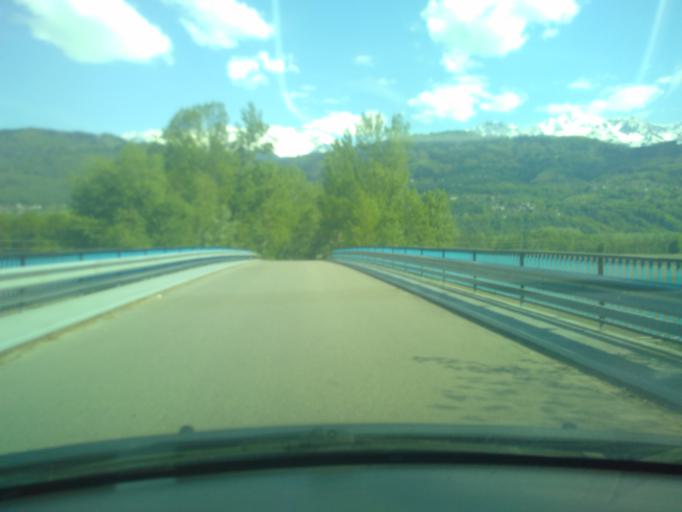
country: FR
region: Rhone-Alpes
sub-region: Departement de l'Isere
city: Froges
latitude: 45.2825
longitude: 5.9101
